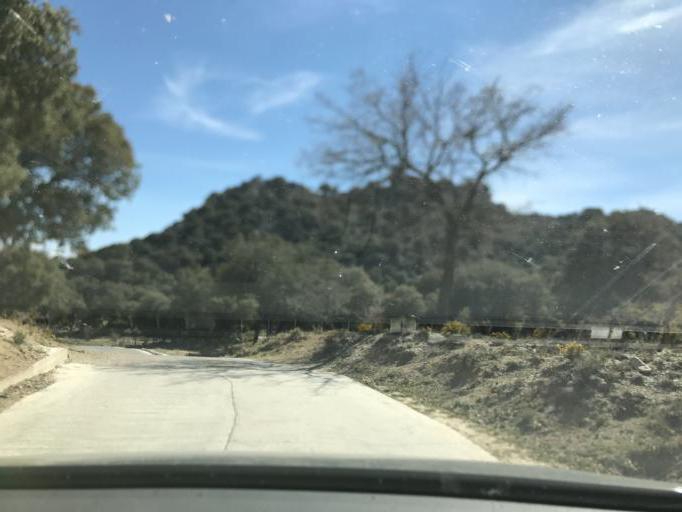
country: ES
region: Andalusia
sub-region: Provincia de Granada
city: Iznalloz
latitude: 37.3182
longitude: -3.4601
